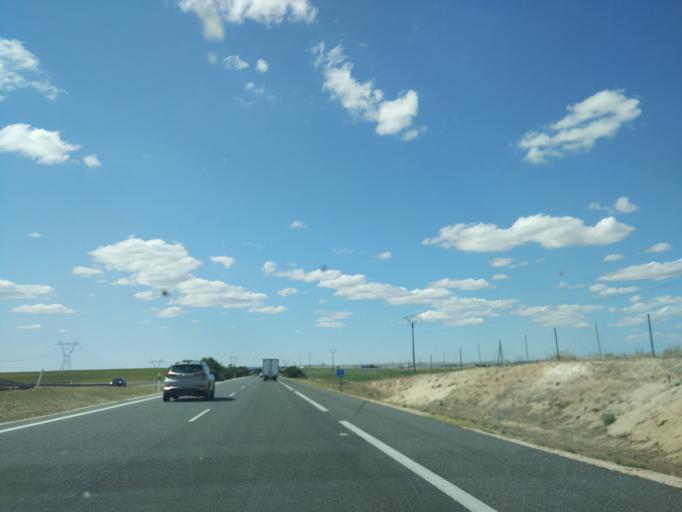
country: ES
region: Castille and Leon
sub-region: Provincia de Valladolid
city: San Vicente del Palacio
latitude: 41.2280
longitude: -4.8500
